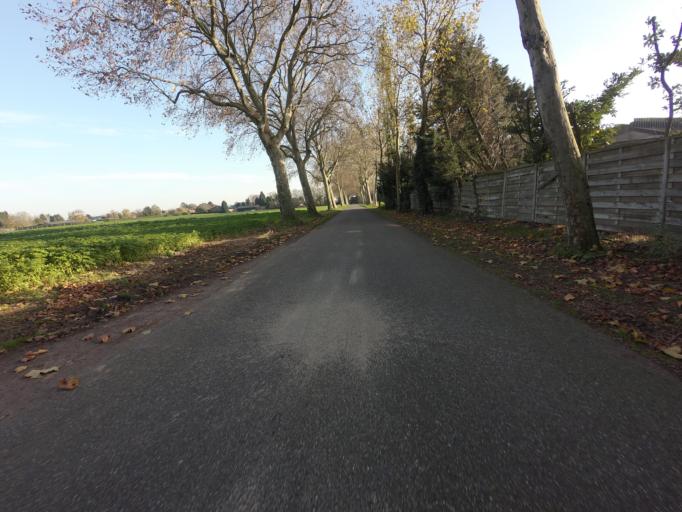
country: NL
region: Limburg
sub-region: Gemeente Echt-Susteren
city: Koningsbosch
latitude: 51.0588
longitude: 5.9421
